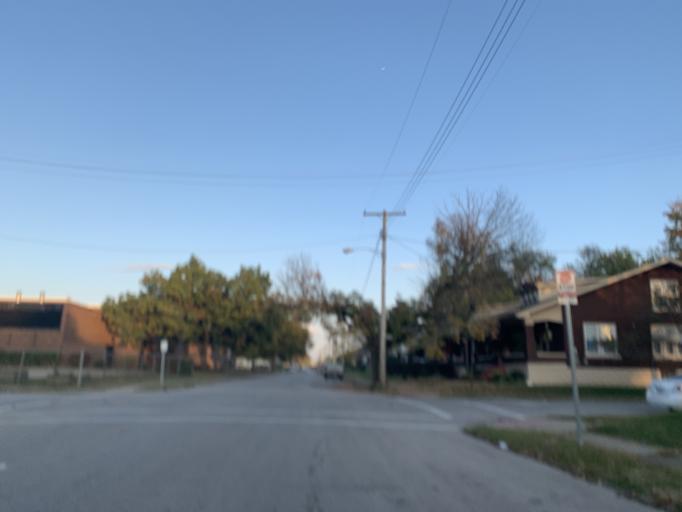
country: US
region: Indiana
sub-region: Floyd County
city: New Albany
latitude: 38.2560
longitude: -85.8114
